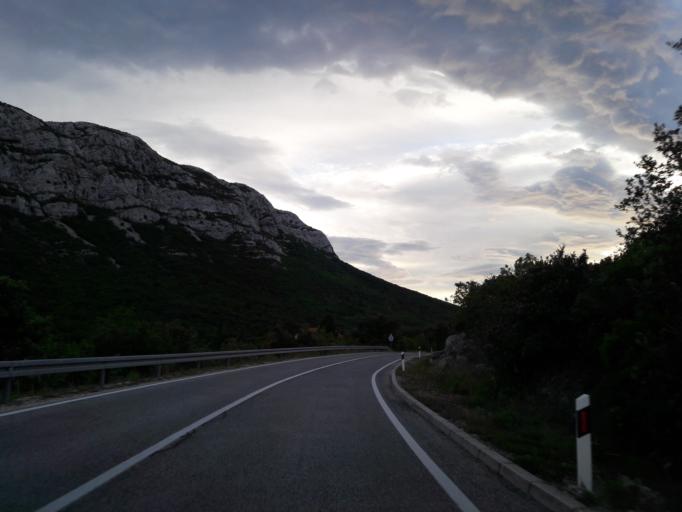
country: BA
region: Federation of Bosnia and Herzegovina
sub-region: Hercegovacko-Bosanski Kanton
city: Neum
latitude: 42.8626
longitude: 17.5540
